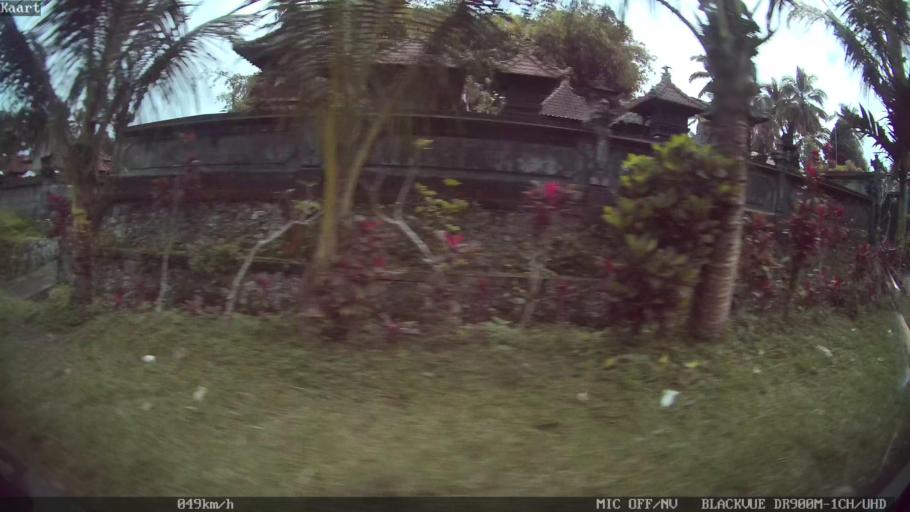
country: ID
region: Bali
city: Banjar Geriana Kangin
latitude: -8.4126
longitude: 115.4380
